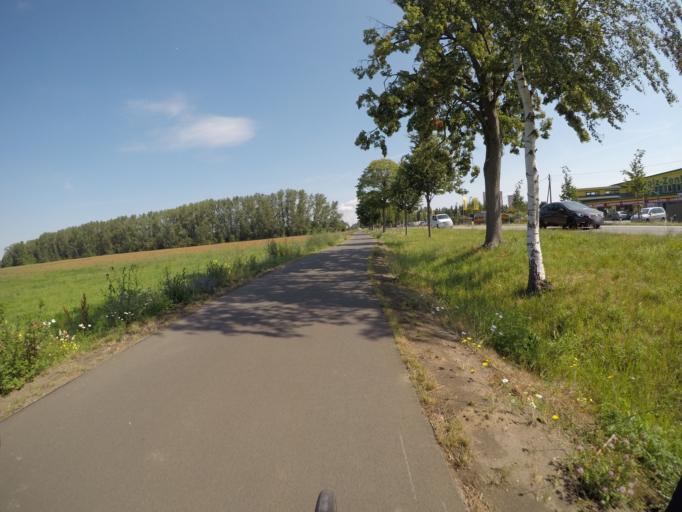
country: DE
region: Brandenburg
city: Bernau bei Berlin
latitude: 52.6589
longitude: 13.5749
